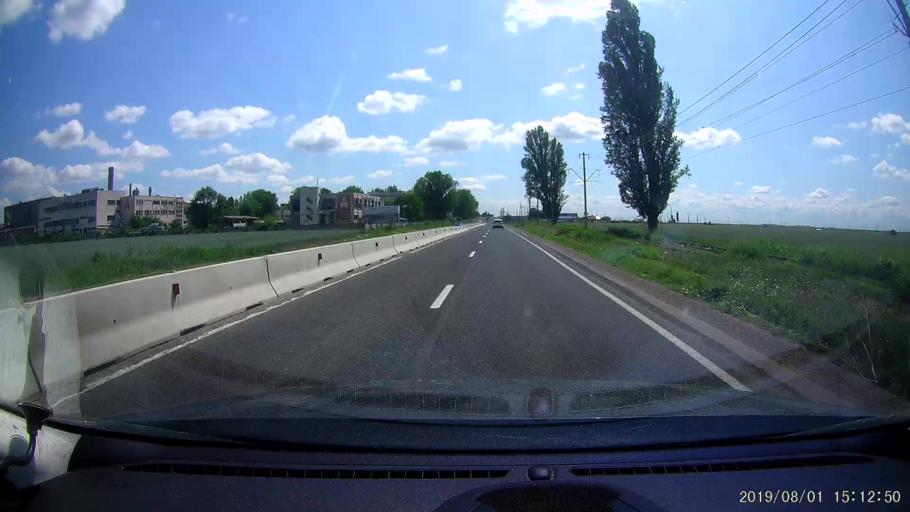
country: RO
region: Braila
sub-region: Comuna Chiscani
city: Lacu Sarat
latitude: 45.2007
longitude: 27.9076
